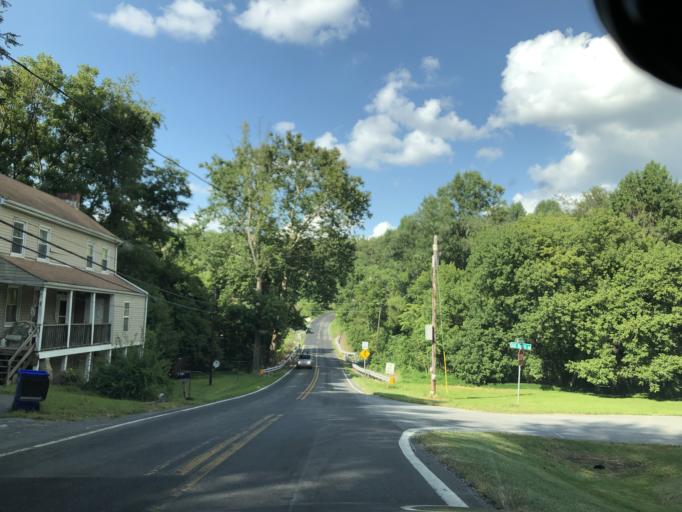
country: US
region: Maryland
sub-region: Carroll County
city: Mount Airy
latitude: 39.4088
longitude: -77.1786
